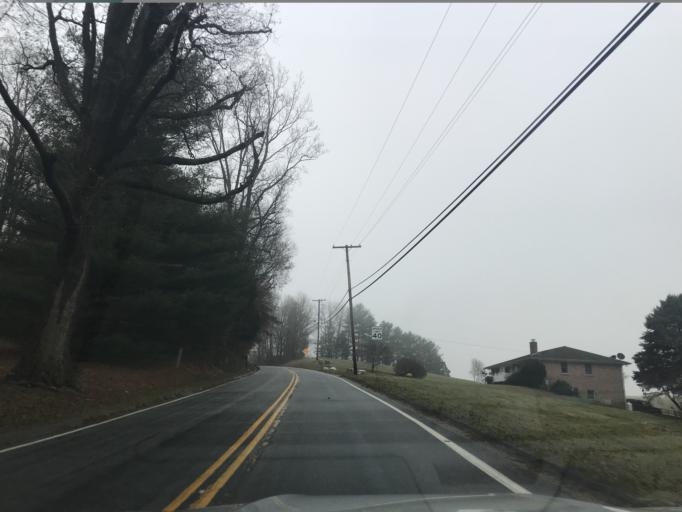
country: US
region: Maryland
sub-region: Harford County
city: South Bel Air
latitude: 39.5741
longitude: -76.2918
